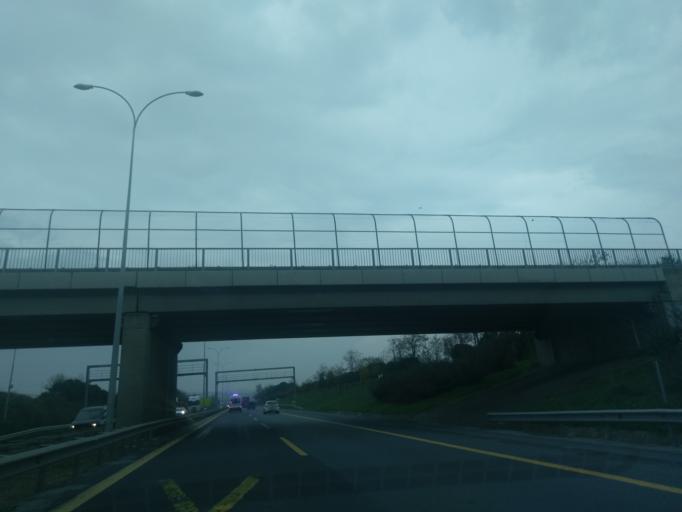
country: TR
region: Istanbul
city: Muratbey
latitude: 41.1065
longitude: 28.5461
